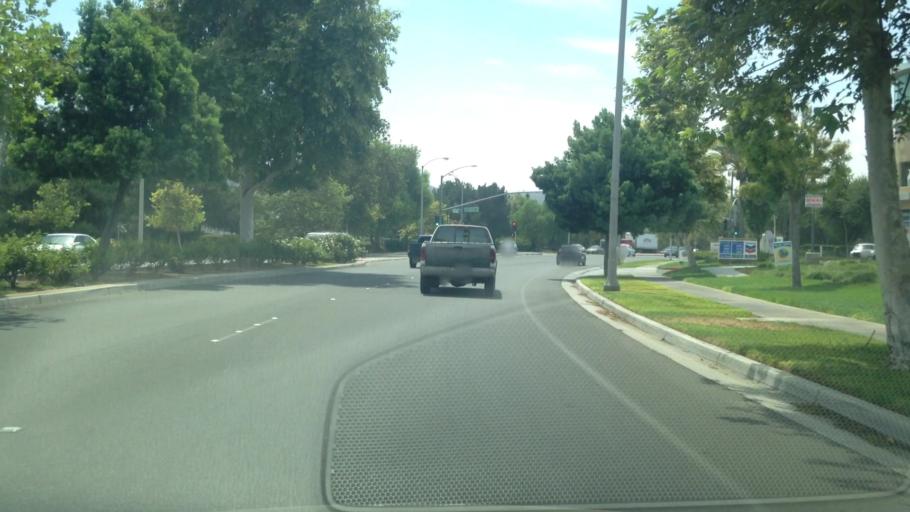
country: US
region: California
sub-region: Riverside County
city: Home Gardens
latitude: 33.9049
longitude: -117.4936
